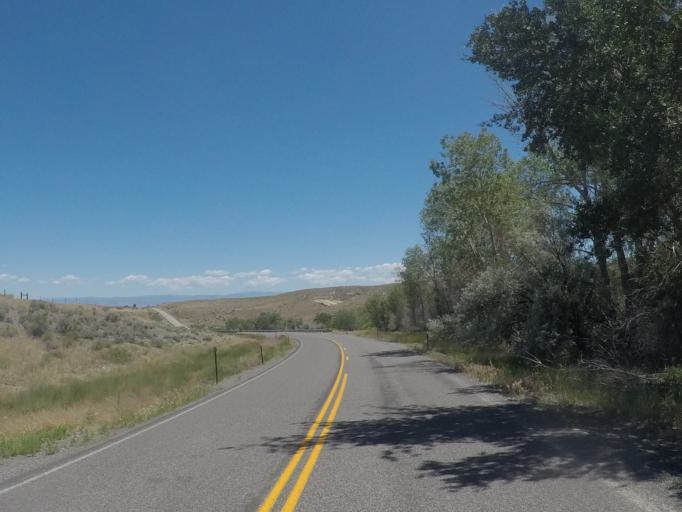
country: US
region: Wyoming
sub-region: Big Horn County
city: Lovell
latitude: 44.7673
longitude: -108.5202
